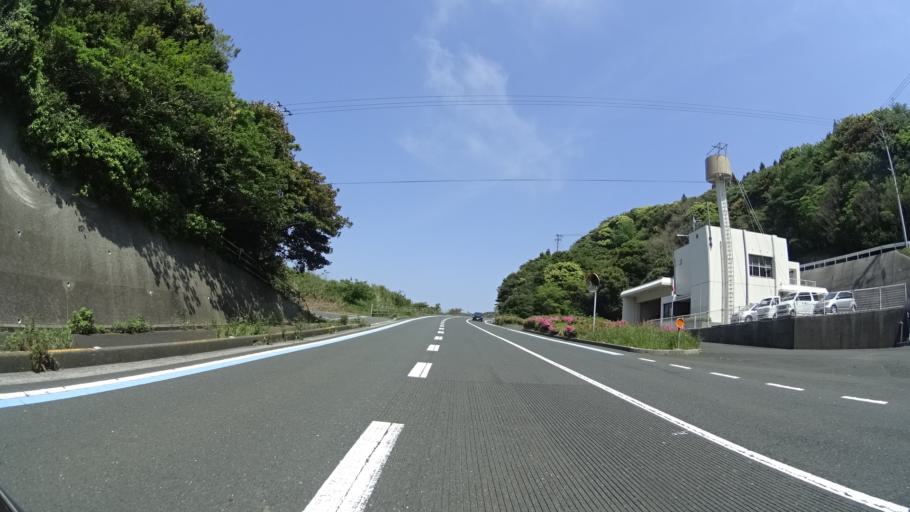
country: JP
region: Ehime
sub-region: Nishiuwa-gun
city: Ikata-cho
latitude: 33.4104
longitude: 132.1730
